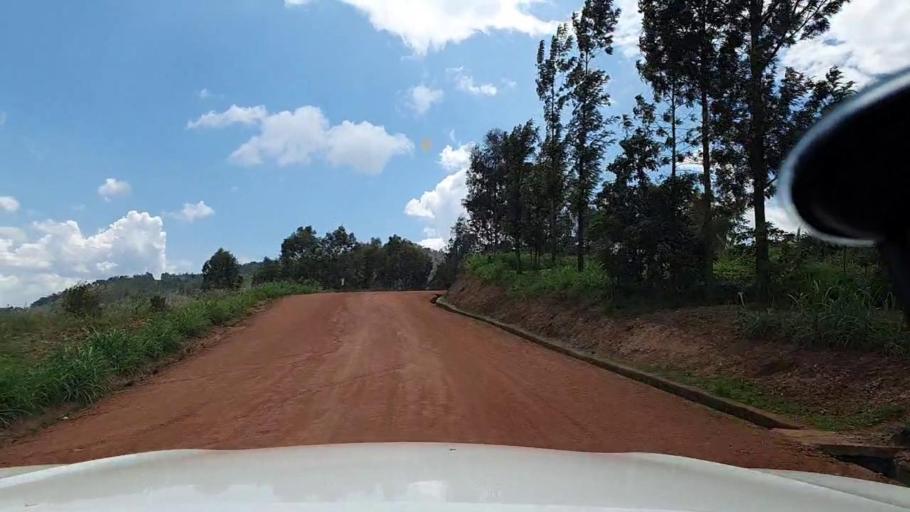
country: RW
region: Kigali
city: Kigali
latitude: -1.7740
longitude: 29.8420
